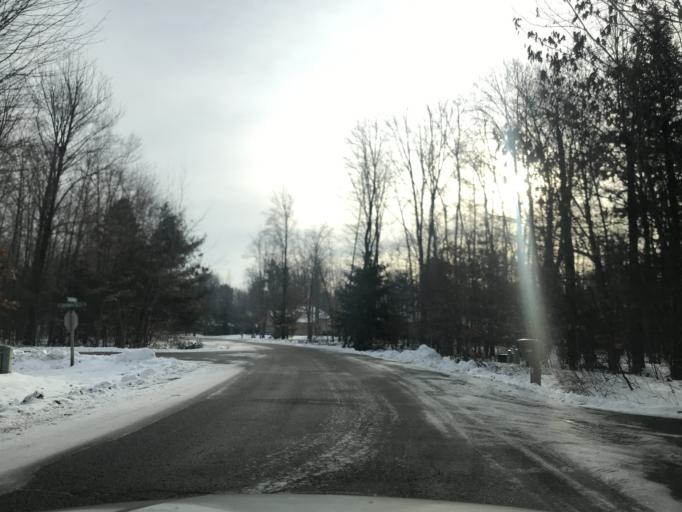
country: US
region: Wisconsin
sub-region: Brown County
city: Suamico
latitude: 44.6861
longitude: -88.0610
